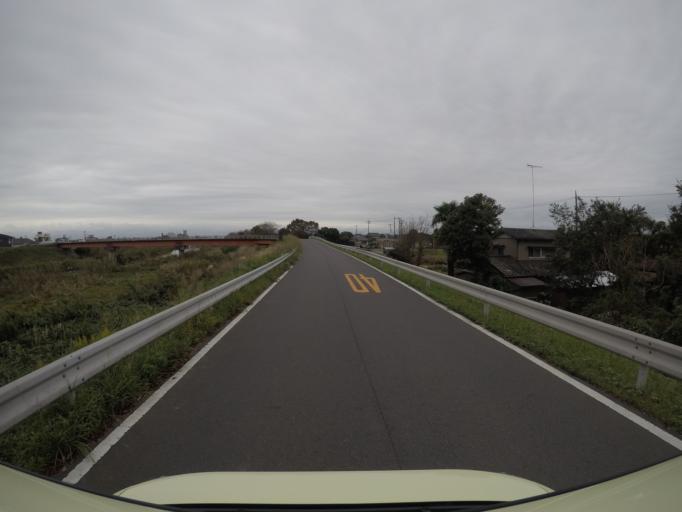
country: JP
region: Ibaraki
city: Naka
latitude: 36.0911
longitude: 140.1727
